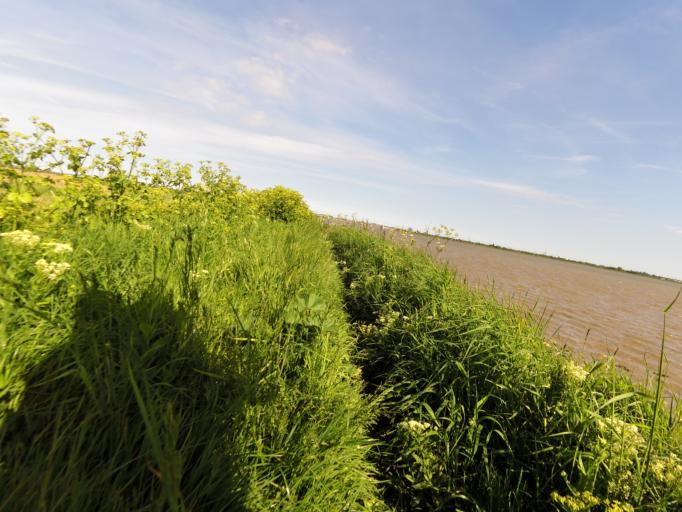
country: GB
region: England
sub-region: Norfolk
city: Great Yarmouth
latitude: 52.6177
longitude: 1.6970
